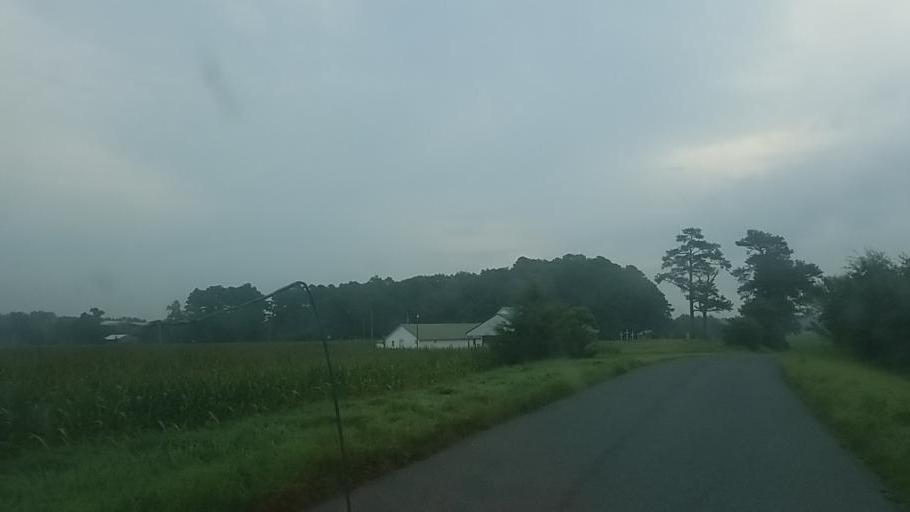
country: US
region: Maryland
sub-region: Wicomico County
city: Pittsville
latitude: 38.4521
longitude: -75.3574
